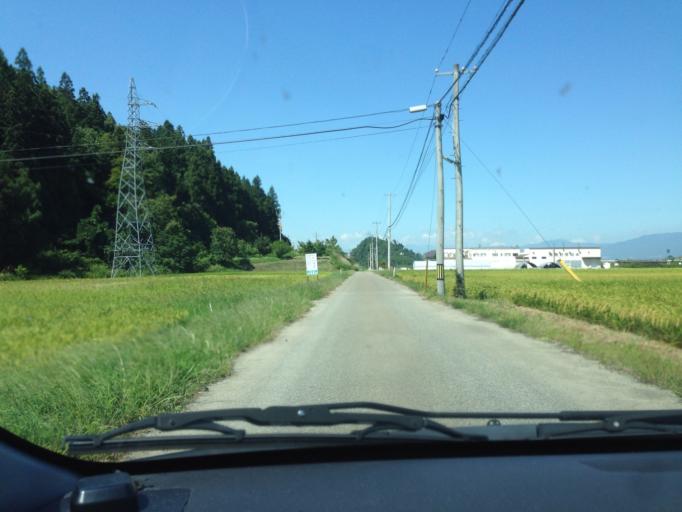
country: JP
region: Fukushima
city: Kitakata
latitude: 37.4326
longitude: 139.8786
